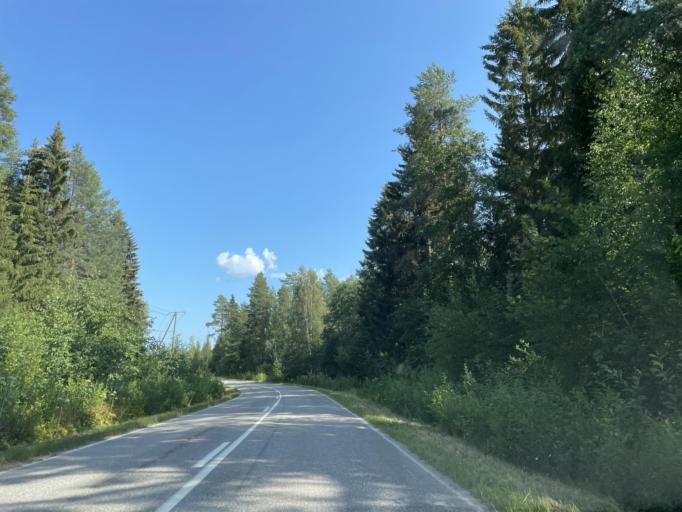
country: FI
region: Central Finland
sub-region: Saarijaervi-Viitasaari
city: Pihtipudas
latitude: 63.3558
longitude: 25.7584
